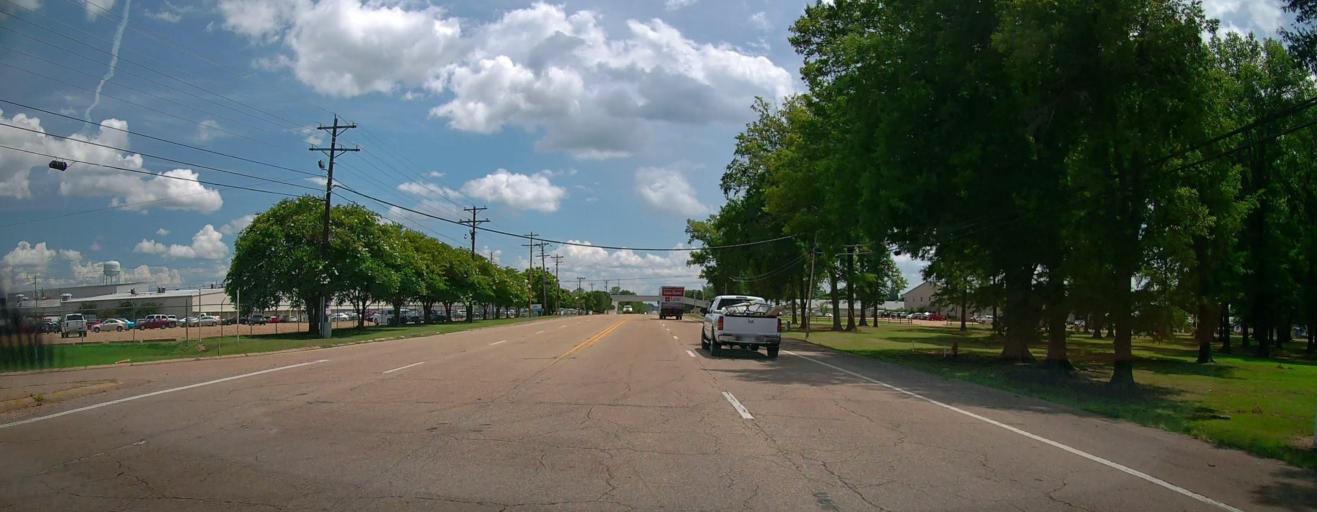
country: US
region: Mississippi
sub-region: Lee County
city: Verona
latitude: 34.1639
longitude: -88.7195
